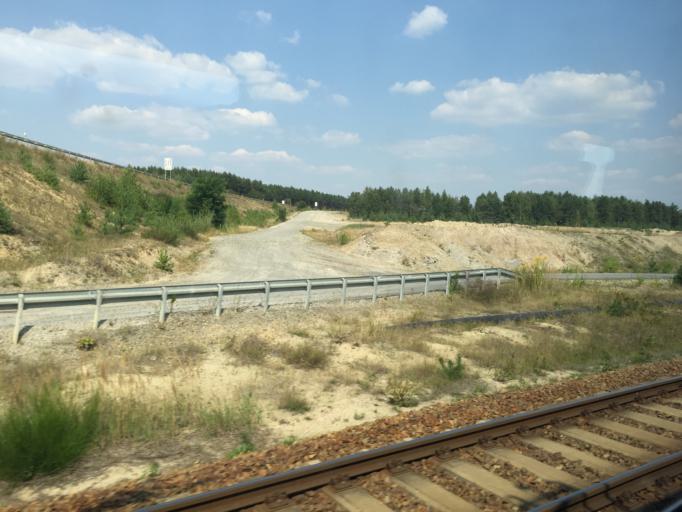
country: DE
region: Brandenburg
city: Senftenberg
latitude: 51.5085
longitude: 13.9575
